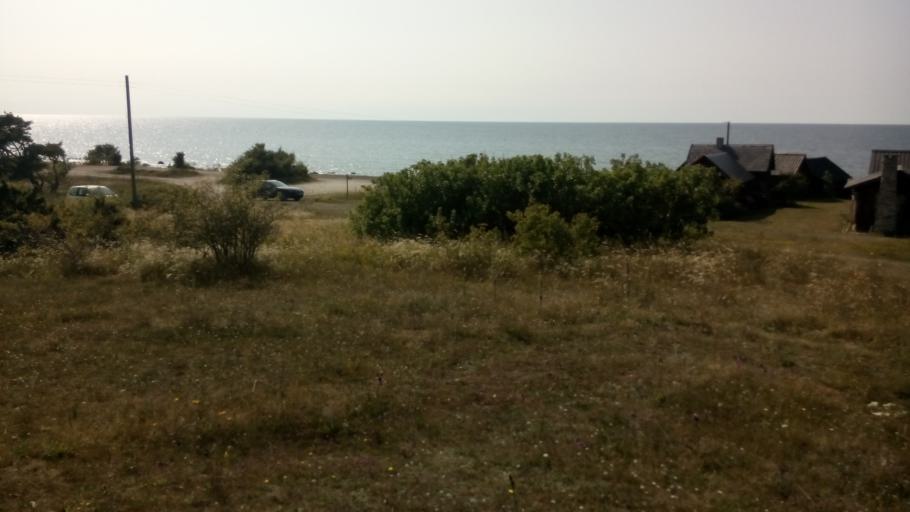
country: SE
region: Gotland
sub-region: Gotland
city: Visby
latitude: 57.7626
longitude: 18.4157
